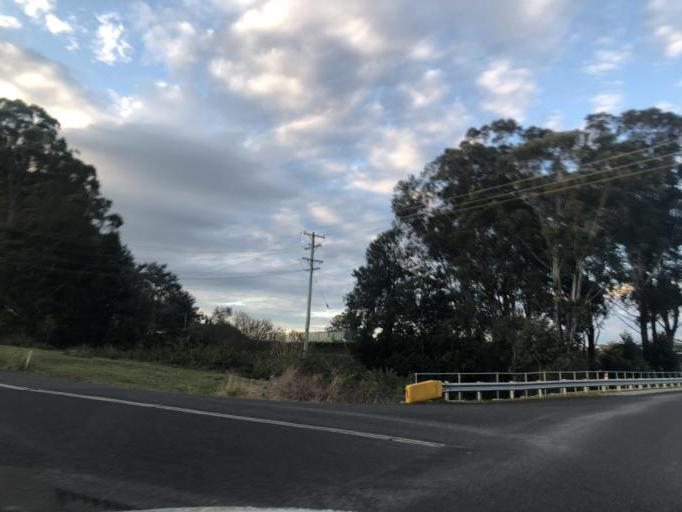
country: AU
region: New South Wales
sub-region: Nambucca Shire
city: Macksville
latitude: -30.7285
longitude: 152.9161
